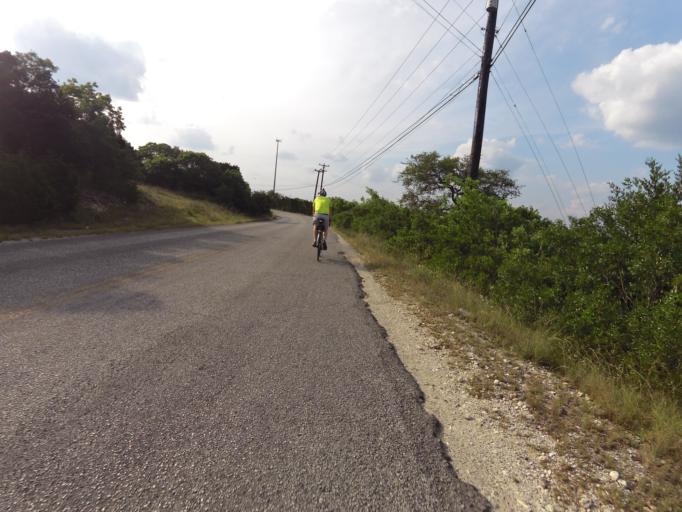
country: US
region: Texas
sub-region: Bexar County
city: Cross Mountain
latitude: 29.6602
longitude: -98.6303
